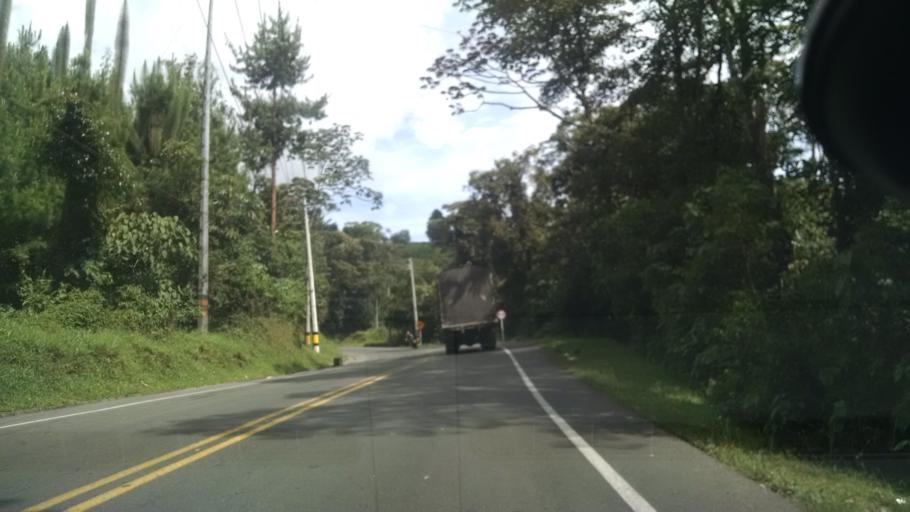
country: CO
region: Antioquia
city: Caldas
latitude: 6.0358
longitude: -75.6253
